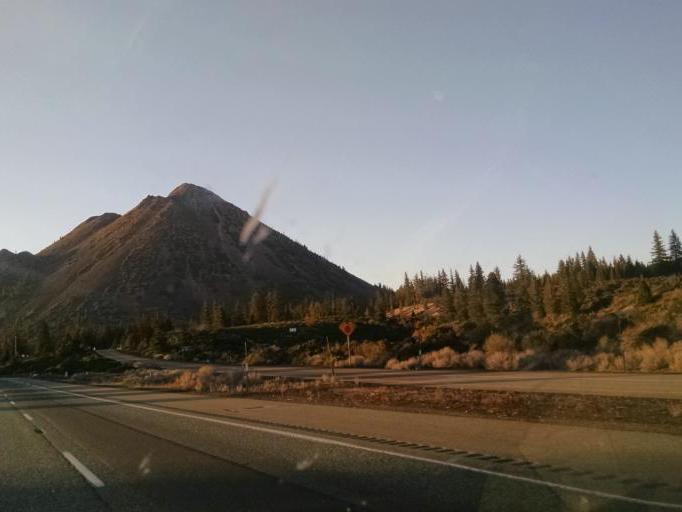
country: US
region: California
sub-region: Siskiyou County
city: Mount Shasta
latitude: 41.3417
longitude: -122.3407
